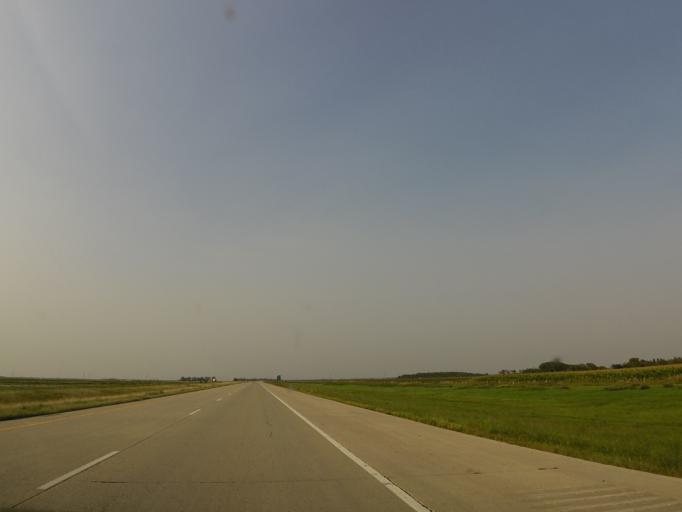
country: US
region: North Dakota
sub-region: Cass County
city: Horace
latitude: 46.6078
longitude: -96.8234
